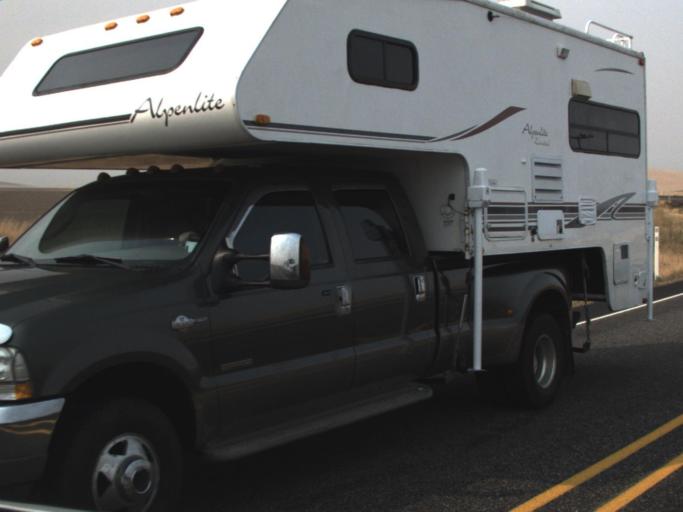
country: US
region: Washington
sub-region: Benton County
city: Benton City
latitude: 46.1837
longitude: -119.6009
